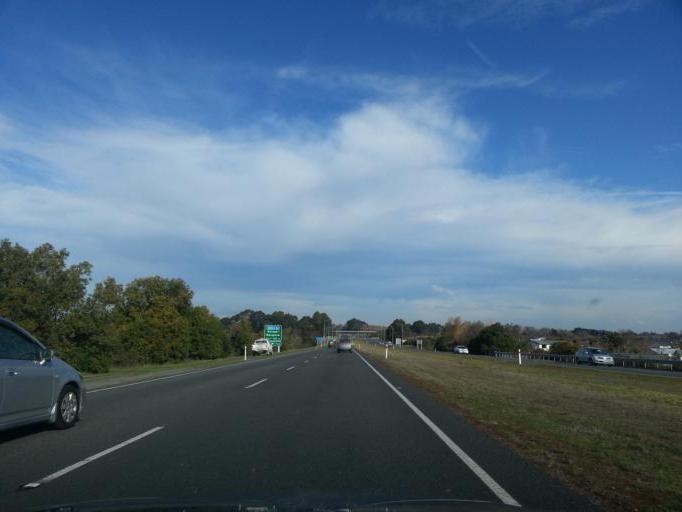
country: NZ
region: Canterbury
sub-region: Waimakariri District
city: Kaiapoi
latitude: -43.3801
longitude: 172.6442
